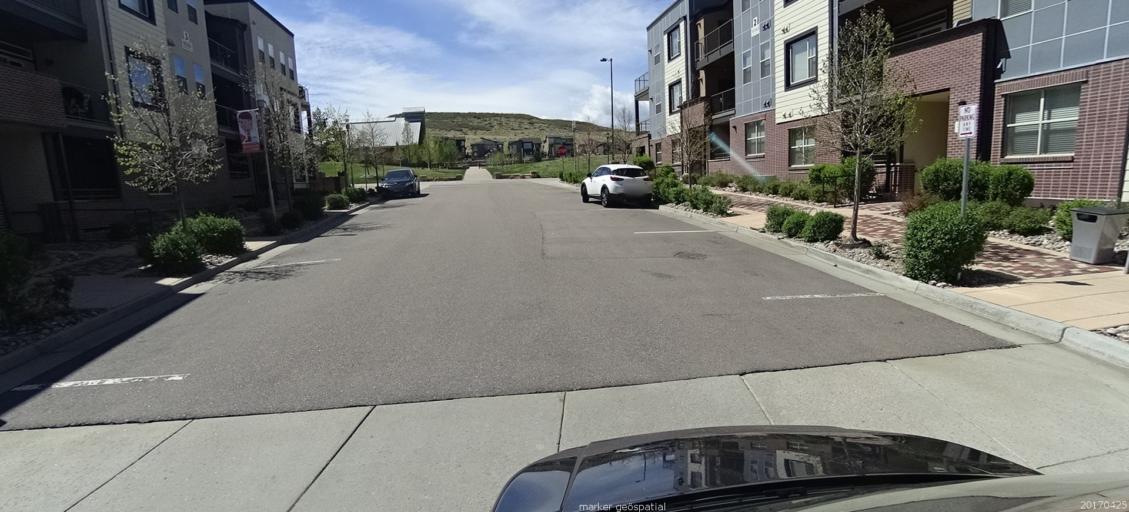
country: US
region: Colorado
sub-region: Douglas County
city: Carriage Club
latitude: 39.5287
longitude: -104.8784
